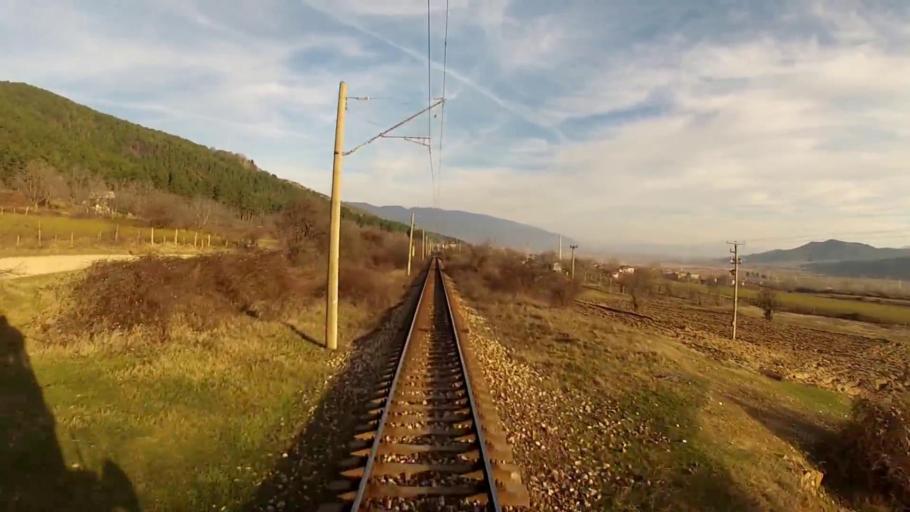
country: BG
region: Plovdiv
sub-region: Obshtina Karlovo
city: Klisura
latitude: 42.7202
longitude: 24.5847
